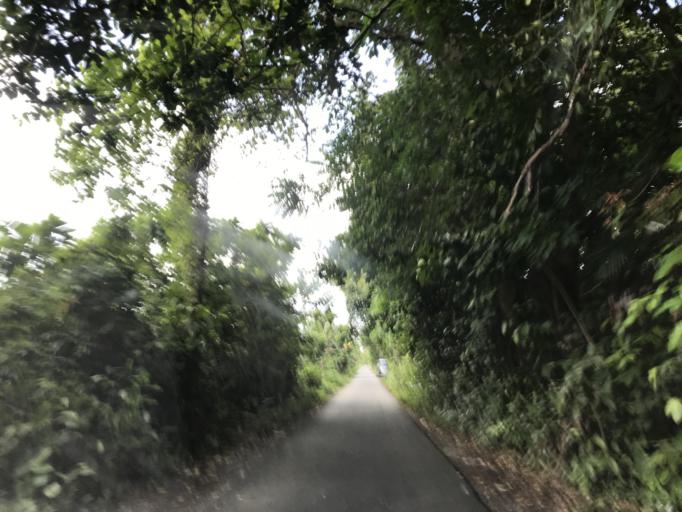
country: MY
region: Kelantan
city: Kota Bharu
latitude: 6.1098
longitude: 102.1910
